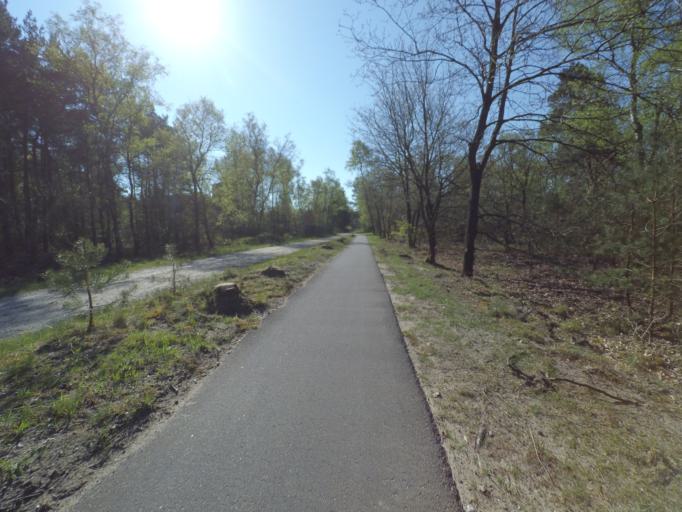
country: NL
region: Gelderland
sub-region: Gemeente Apeldoorn
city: Uddel
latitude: 52.1867
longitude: 5.8097
